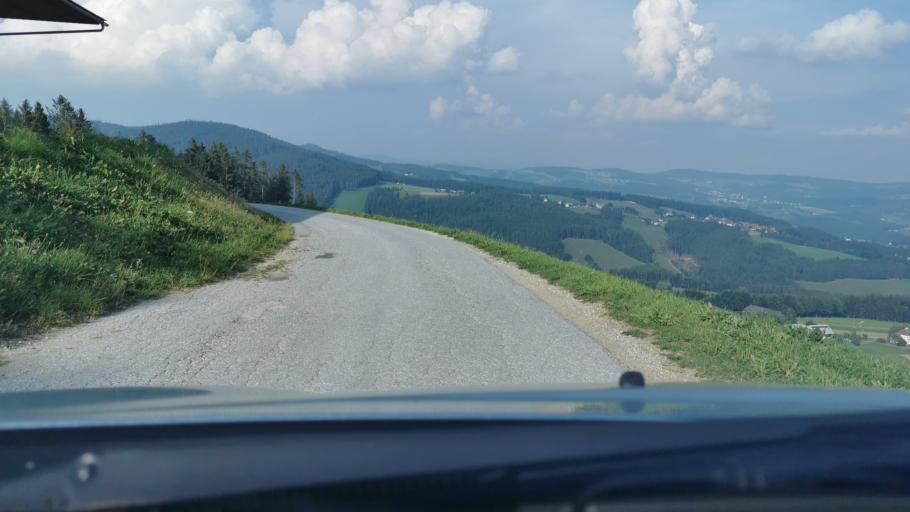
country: AT
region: Styria
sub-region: Politischer Bezirk Weiz
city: Fischbach
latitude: 47.3863
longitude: 15.6429
